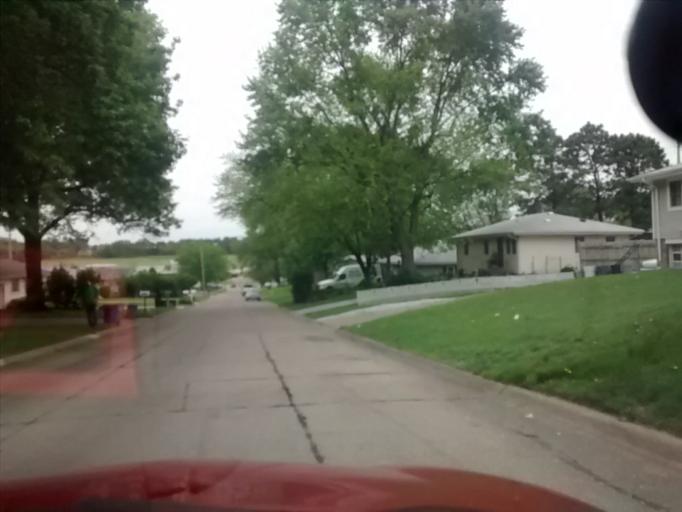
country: US
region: Nebraska
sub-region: Sarpy County
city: Bellevue
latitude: 41.1718
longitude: -95.9222
